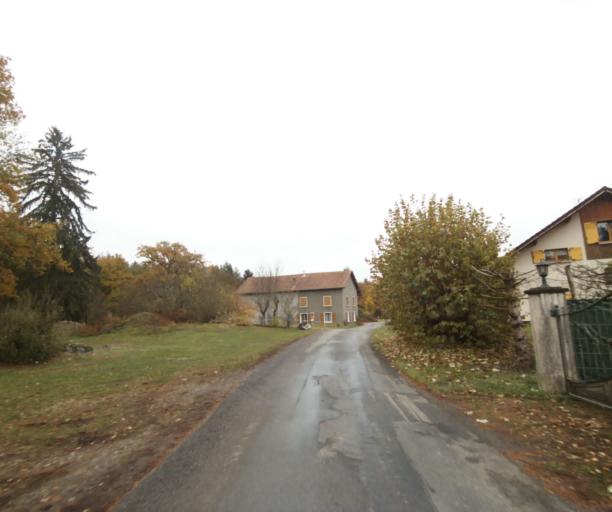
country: FR
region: Rhone-Alpes
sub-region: Departement de la Haute-Savoie
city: Reignier-Esery
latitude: 46.1242
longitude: 6.2903
